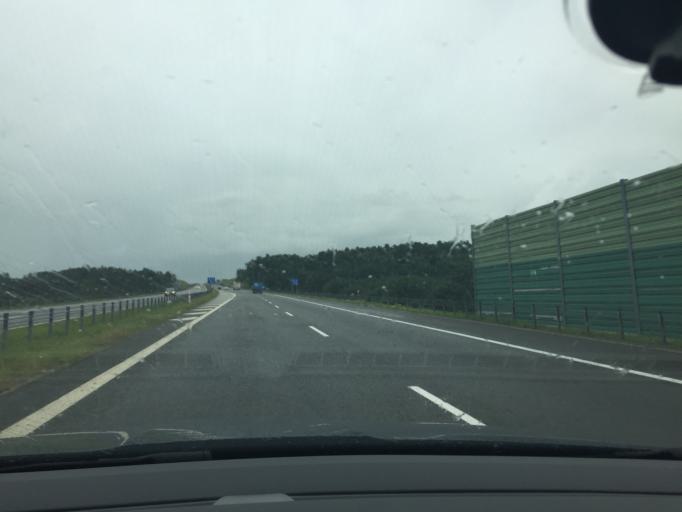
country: PL
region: Kujawsko-Pomorskie
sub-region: Powiat chelminski
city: Lisewo
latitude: 53.3992
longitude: 18.6841
